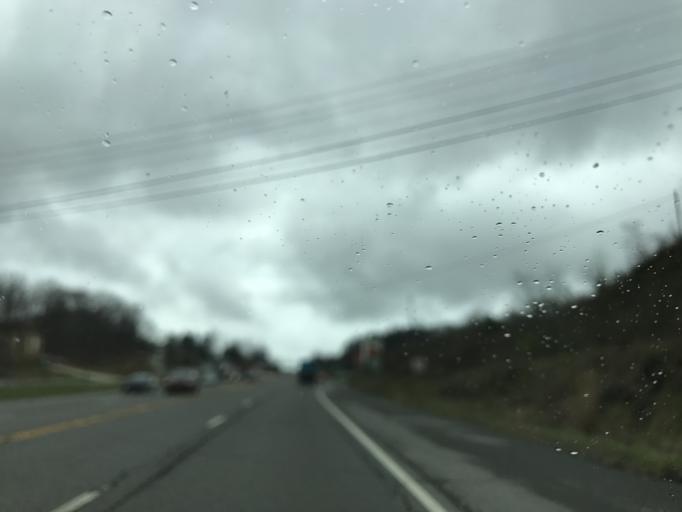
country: US
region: West Virginia
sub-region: Raleigh County
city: Prosperity
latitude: 37.8498
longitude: -81.1964
